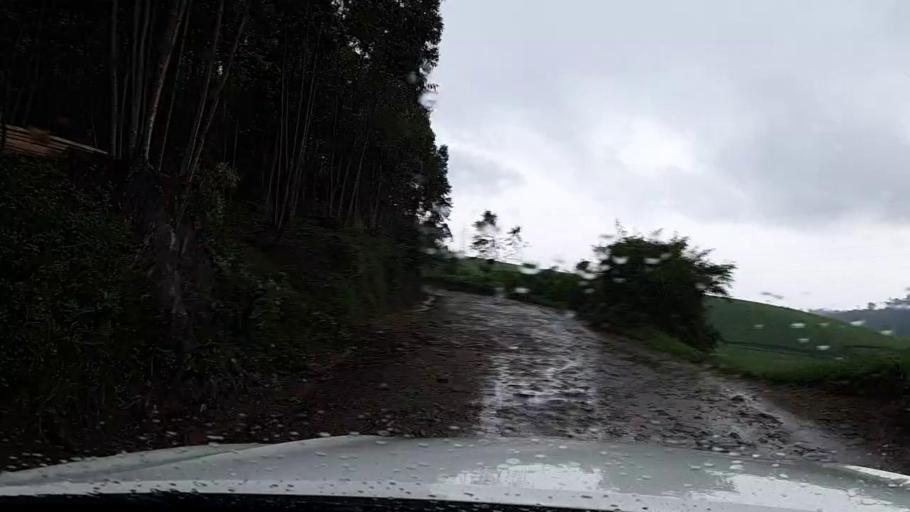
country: RW
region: Western Province
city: Cyangugu
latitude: -2.4614
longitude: 29.0366
